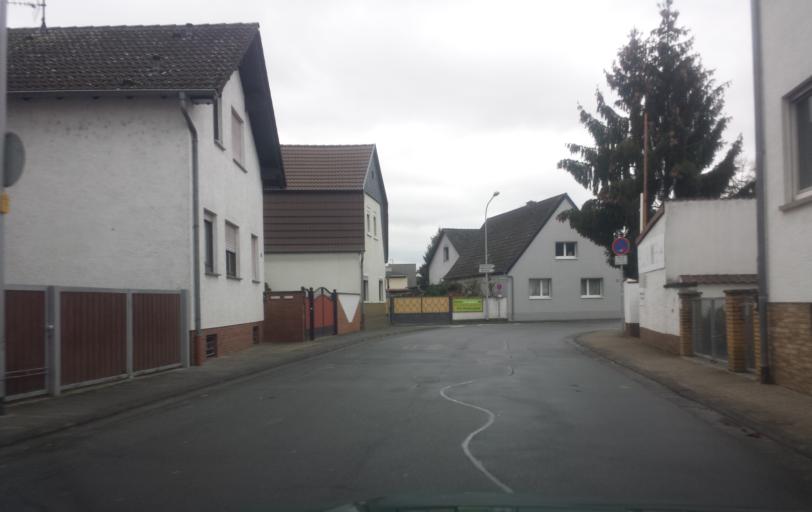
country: DE
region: Hesse
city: Weiterstadt
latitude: 49.9135
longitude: 8.5700
